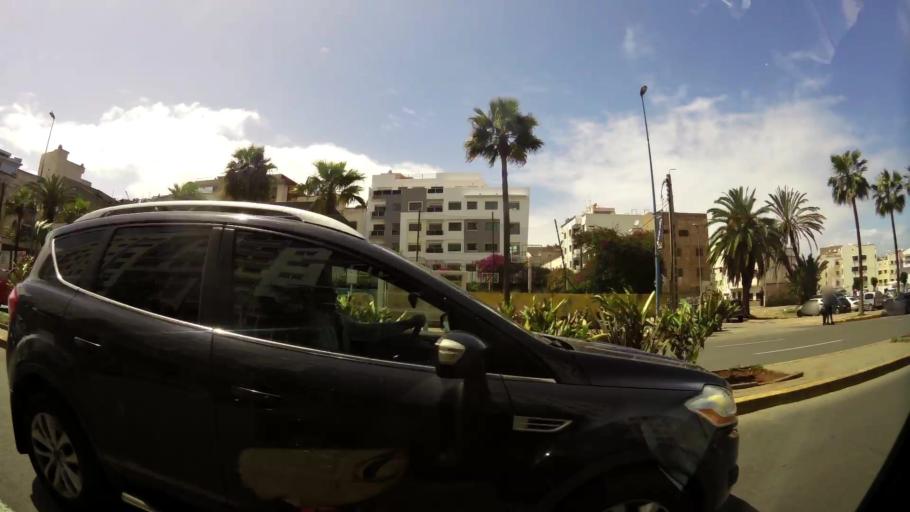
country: MA
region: Grand Casablanca
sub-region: Casablanca
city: Casablanca
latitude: 33.5995
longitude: -7.6388
